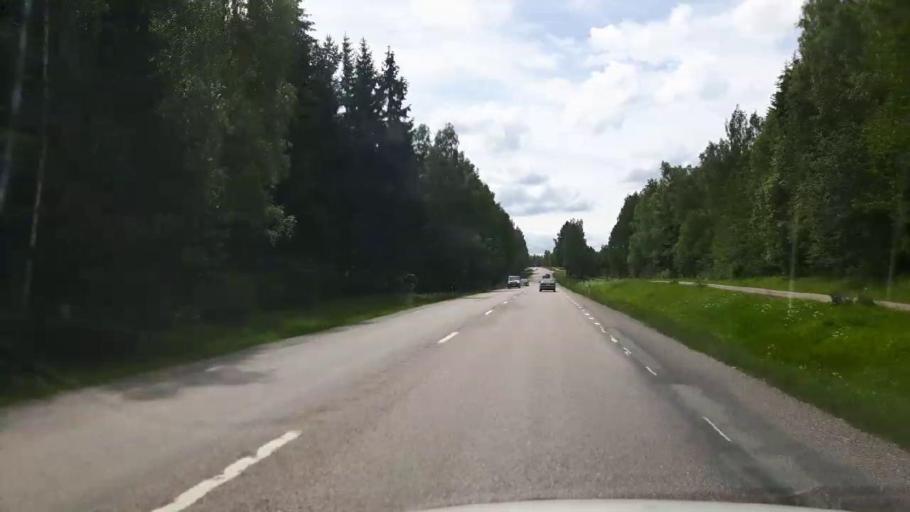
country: SE
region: Vaestmanland
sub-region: Fagersta Kommun
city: Fagersta
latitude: 59.9706
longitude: 15.7765
